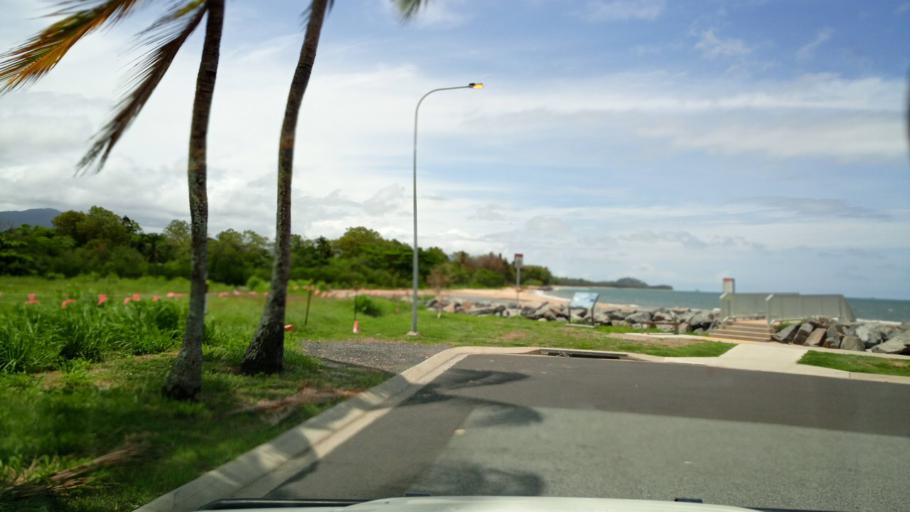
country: AU
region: Queensland
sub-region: Cairns
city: Yorkeys Knob
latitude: -16.8463
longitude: 145.7459
